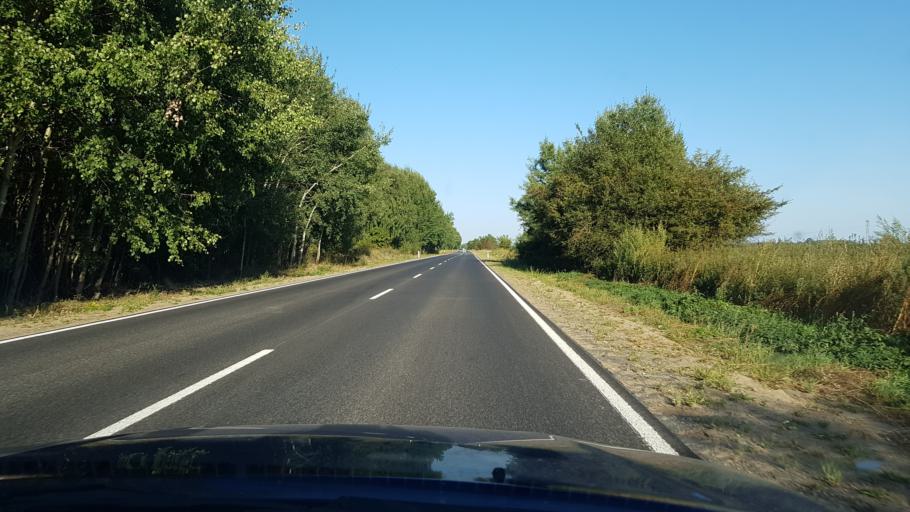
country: PL
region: West Pomeranian Voivodeship
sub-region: Powiat stargardzki
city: Stara Dabrowa
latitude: 53.4336
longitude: 15.0936
